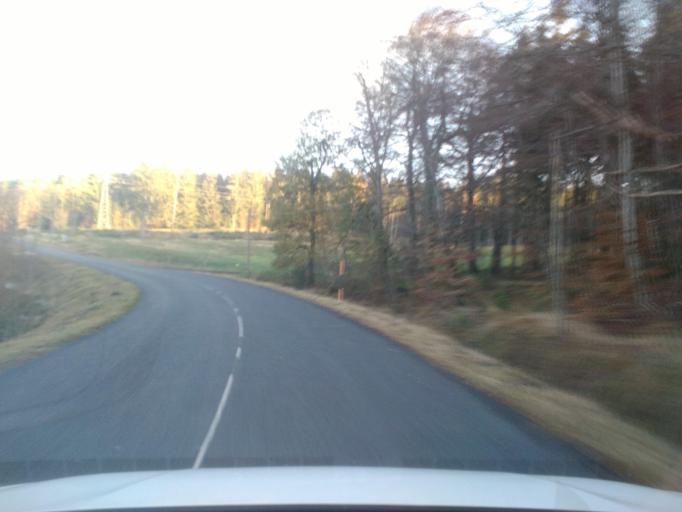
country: FR
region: Lorraine
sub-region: Departement des Vosges
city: Senones
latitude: 48.3809
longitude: 7.0979
